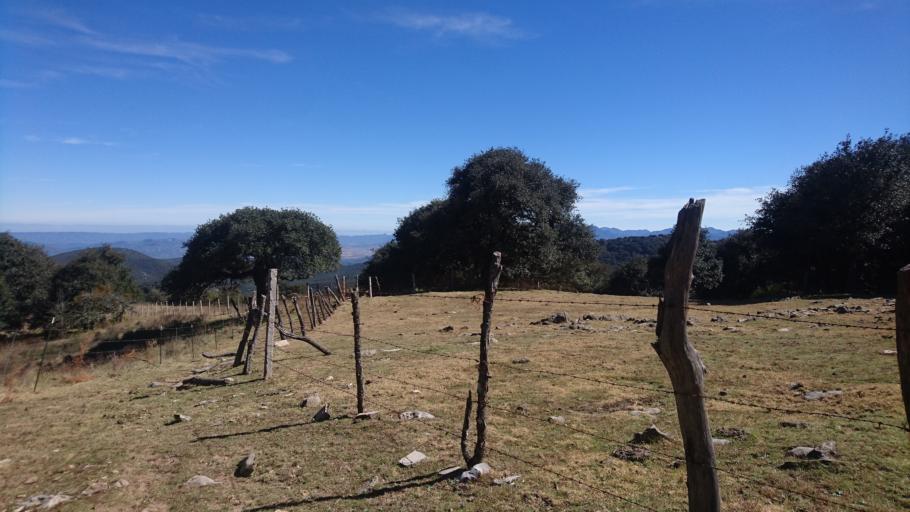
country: MX
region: San Luis Potosi
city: Zaragoza
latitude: 22.0240
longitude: -100.6182
